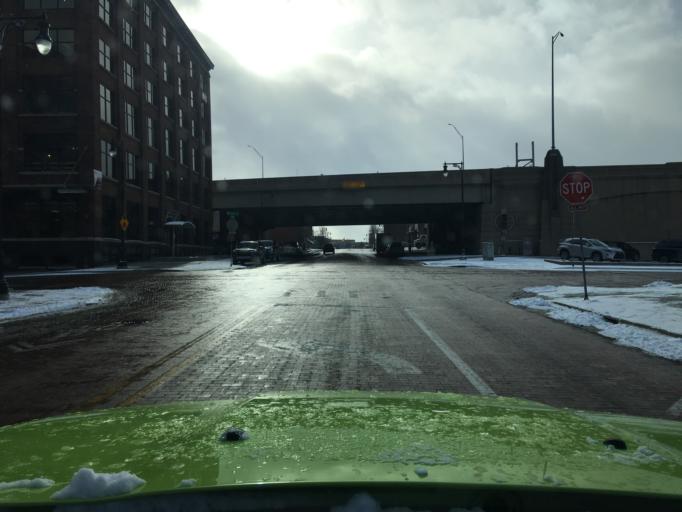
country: US
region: Michigan
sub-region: Kent County
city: Grand Rapids
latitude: 42.9610
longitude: -85.6732
